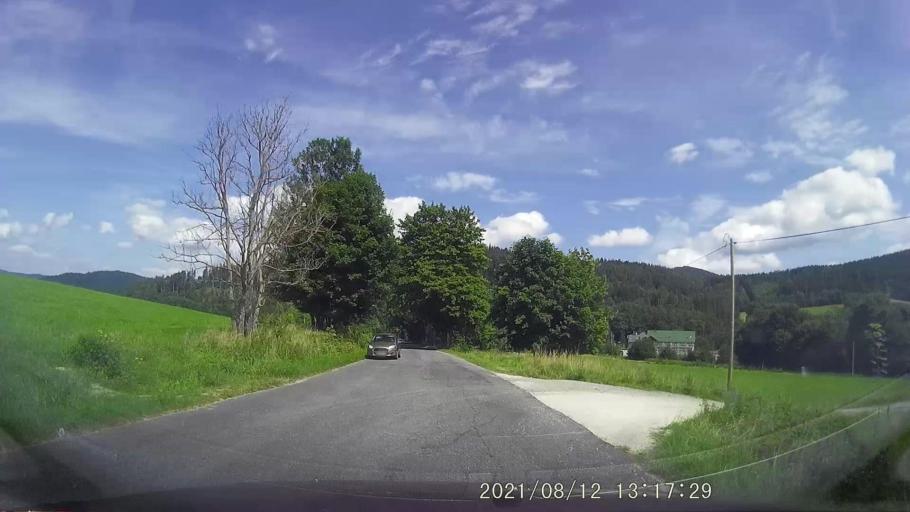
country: PL
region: Lower Silesian Voivodeship
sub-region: Powiat klodzki
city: Stronie Slaskie
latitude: 50.2698
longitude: 16.8836
